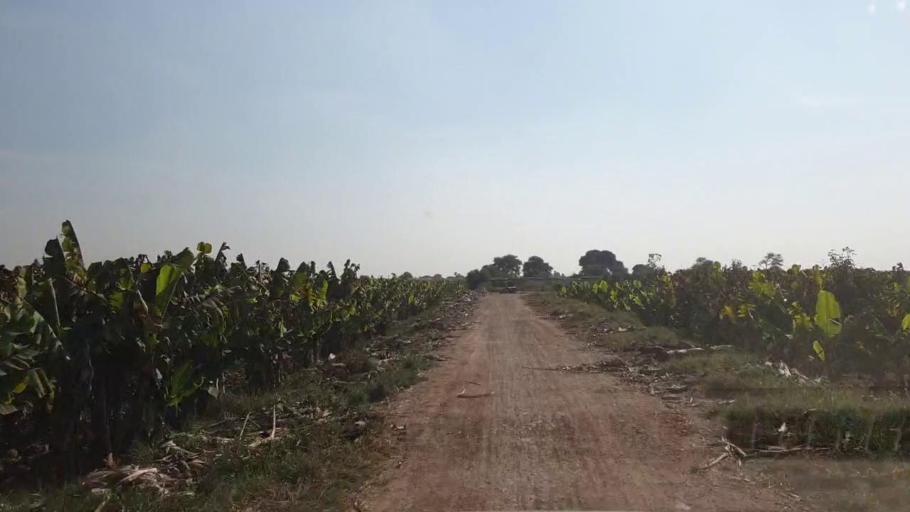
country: PK
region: Sindh
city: Chambar
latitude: 25.3233
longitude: 68.7938
